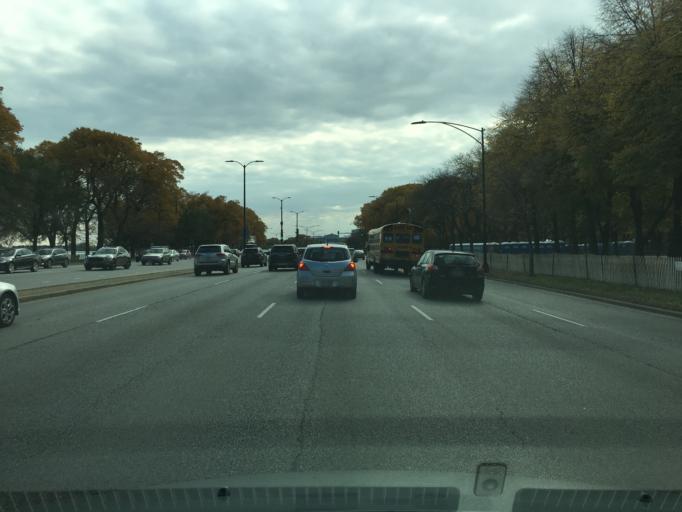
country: US
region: Illinois
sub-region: Cook County
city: Chicago
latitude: 41.8795
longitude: -87.6175
